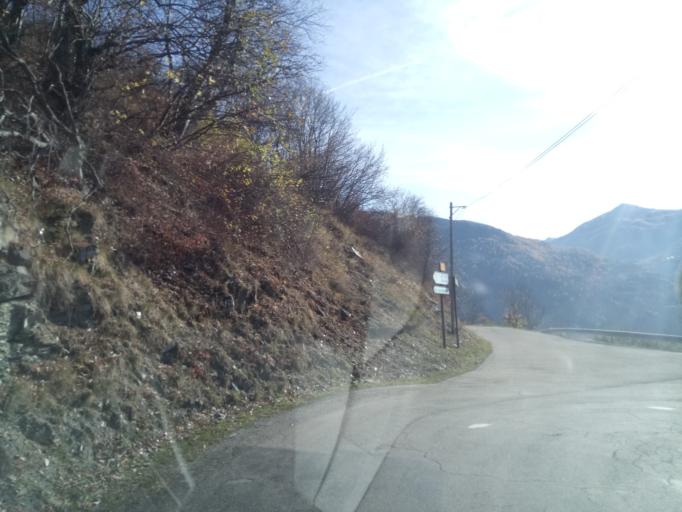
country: FR
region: Rhone-Alpes
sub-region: Departement de la Savoie
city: Saint-Michel-de-Maurienne
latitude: 45.2242
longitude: 6.4831
